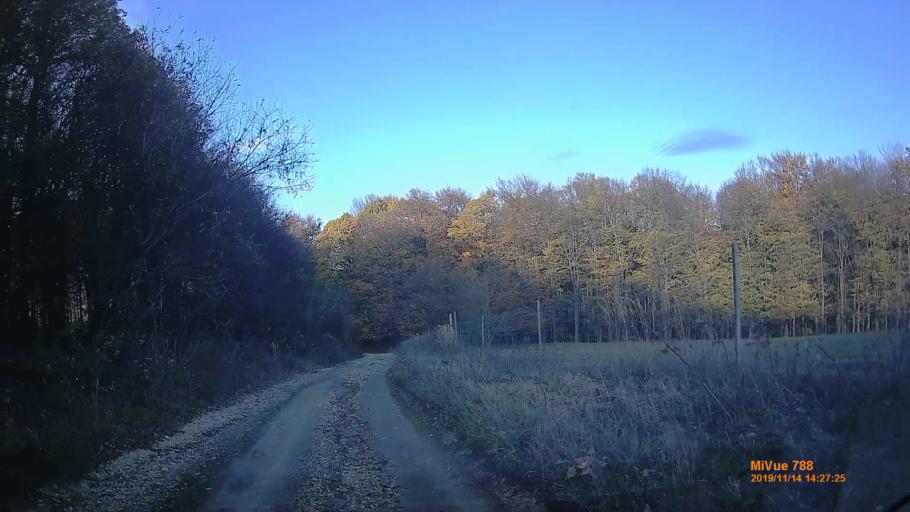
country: HU
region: Veszprem
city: Herend
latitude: 47.2053
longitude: 17.7908
